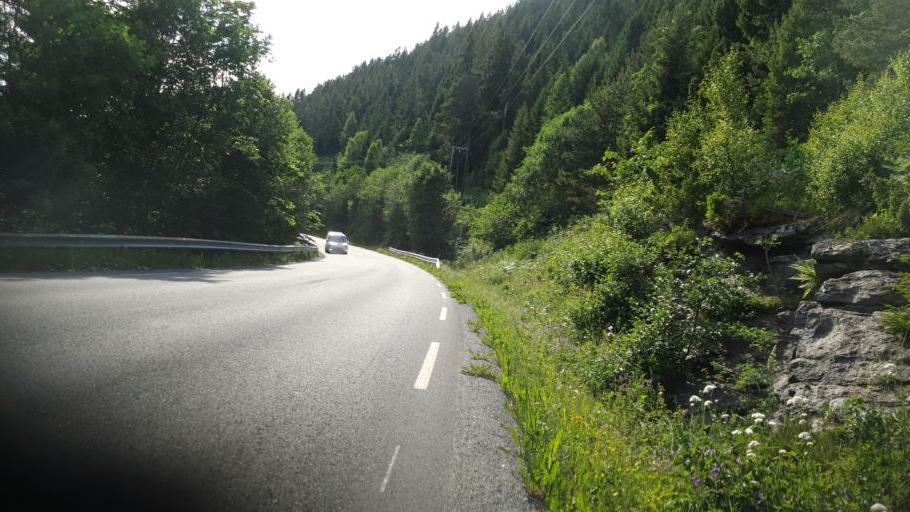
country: NO
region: Sor-Trondelag
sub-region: Trondheim
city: Trondheim
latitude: 63.5577
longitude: 10.2737
